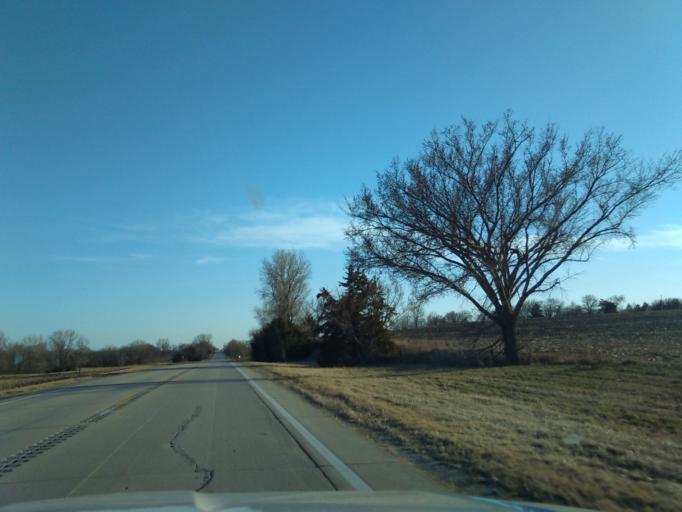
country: US
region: Nebraska
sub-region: Johnson County
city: Tecumseh
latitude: 40.4966
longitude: -96.1798
